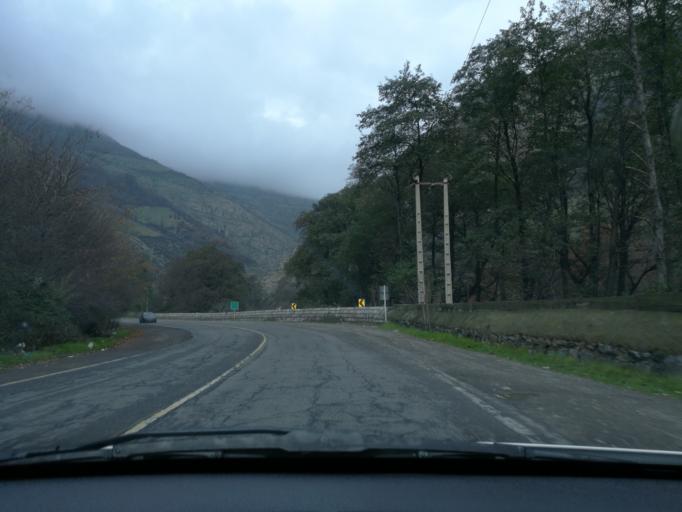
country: IR
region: Mazandaran
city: Chalus
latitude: 36.3599
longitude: 51.2632
